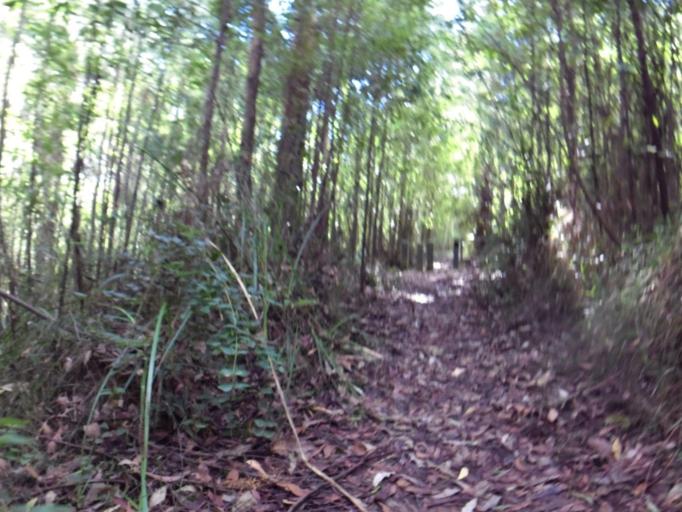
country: AU
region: Victoria
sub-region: Cardinia
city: Bunyip
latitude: -37.9693
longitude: 145.8156
